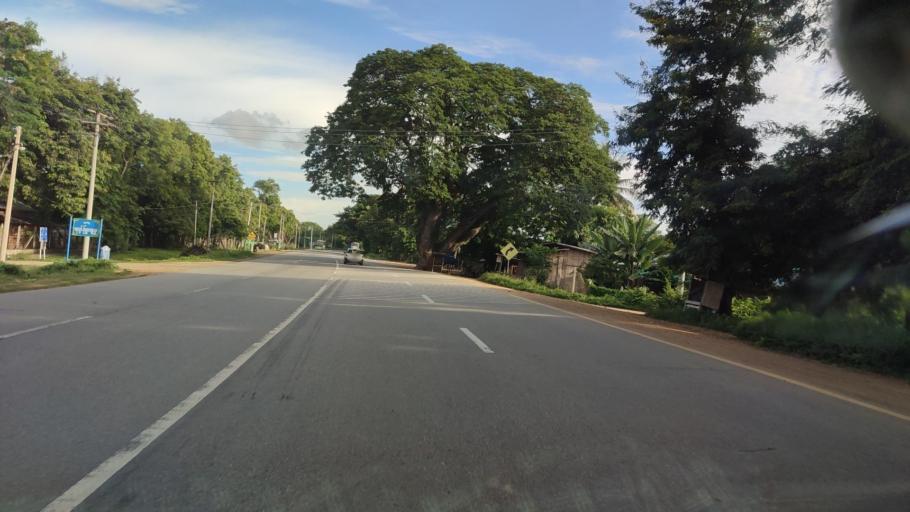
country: MM
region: Mandalay
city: Yamethin
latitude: 20.1798
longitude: 96.1885
